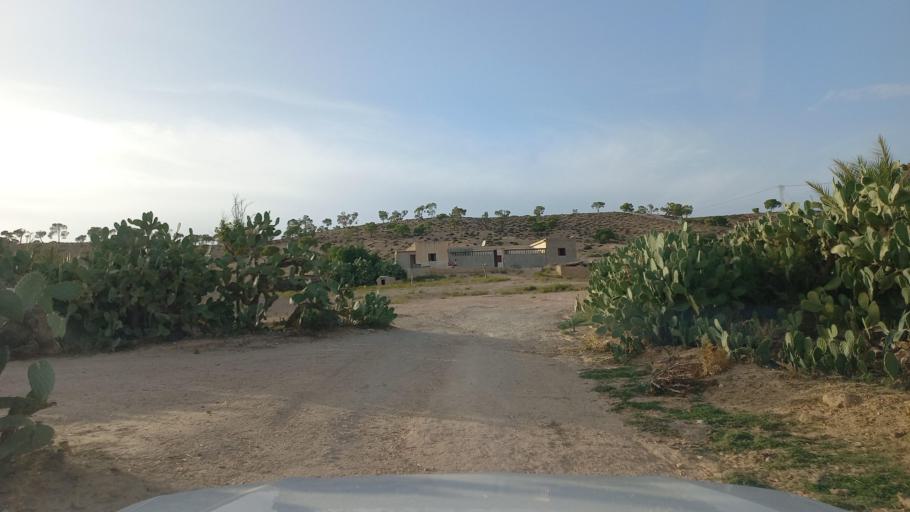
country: TN
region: Al Qasrayn
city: Sbiba
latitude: 35.4060
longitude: 8.8964
